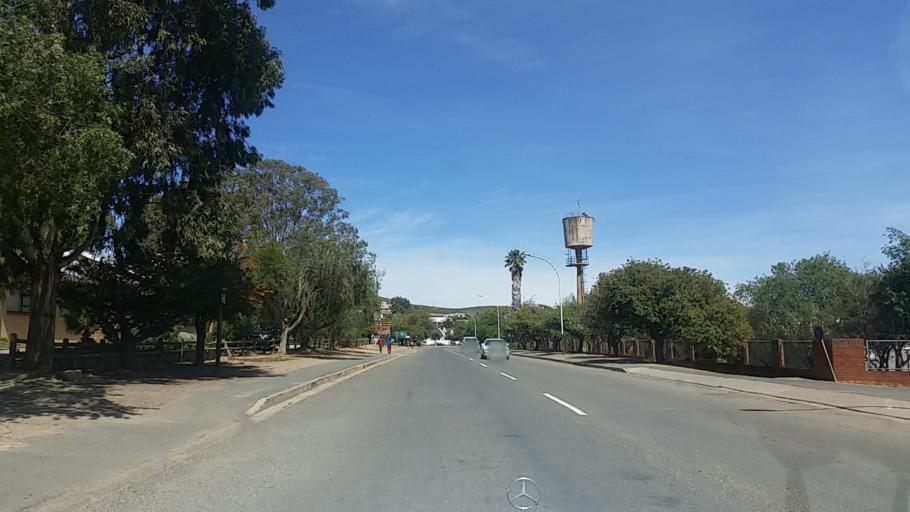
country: ZA
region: Western Cape
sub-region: Eden District Municipality
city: Knysna
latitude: -33.6576
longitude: 23.1248
